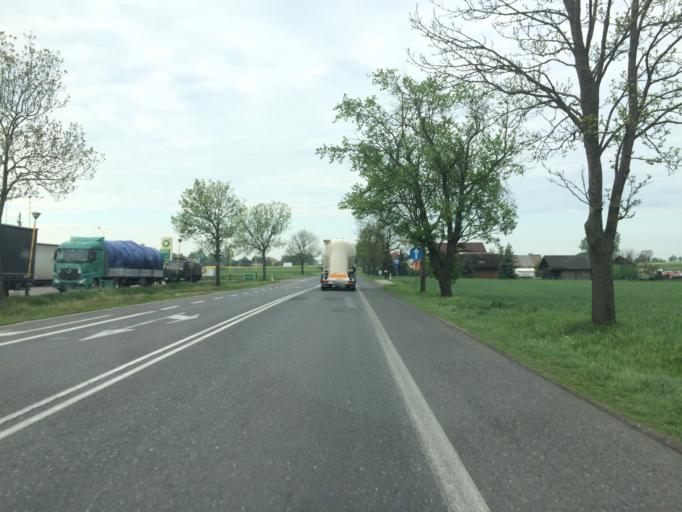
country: PL
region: Masovian Voivodeship
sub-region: Powiat mlawski
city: Wisniewo
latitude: 53.0754
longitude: 20.3522
